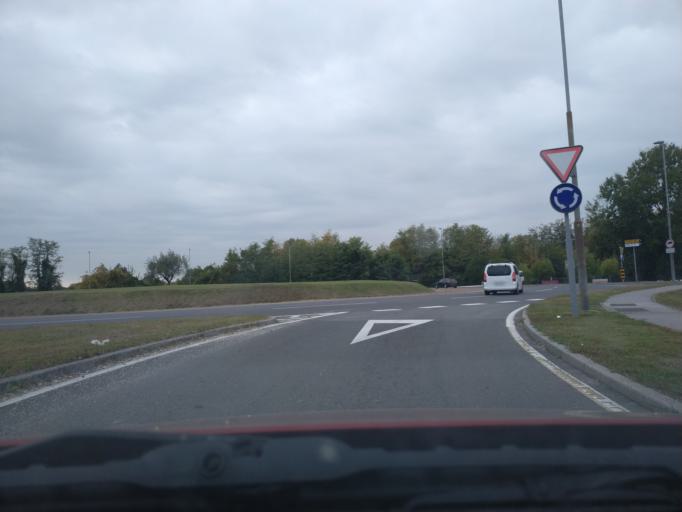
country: SI
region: Sempeter-Vrtojba
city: Sempeter pri Gorici
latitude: 45.9403
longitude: 13.6386
